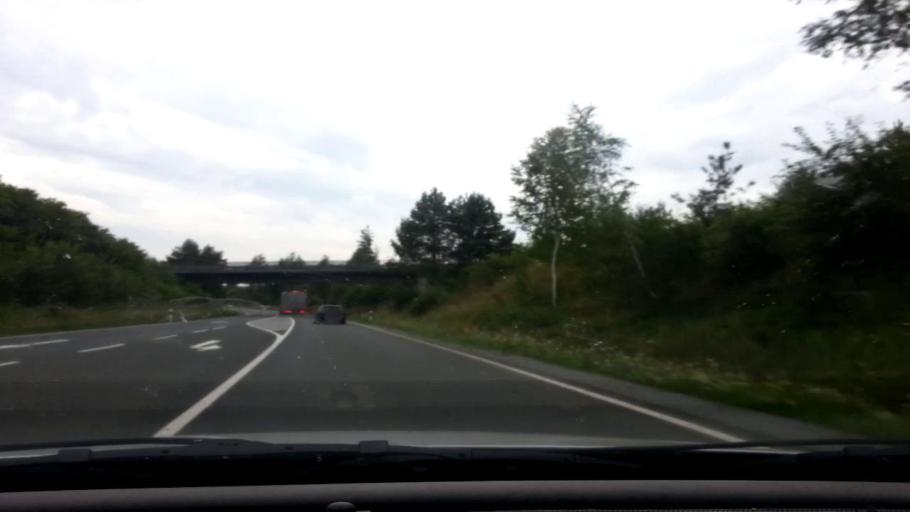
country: DE
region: Bavaria
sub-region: Upper Franconia
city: Seybothenreuth
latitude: 49.8933
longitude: 11.7144
